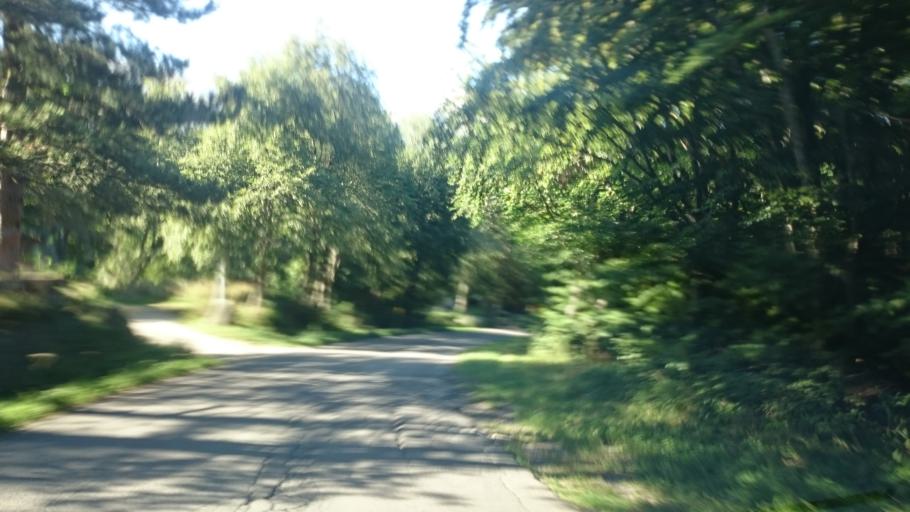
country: IT
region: Emilia-Romagna
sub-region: Provincia di Reggio Emilia
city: Villa Minozzo
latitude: 44.3033
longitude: 10.4280
